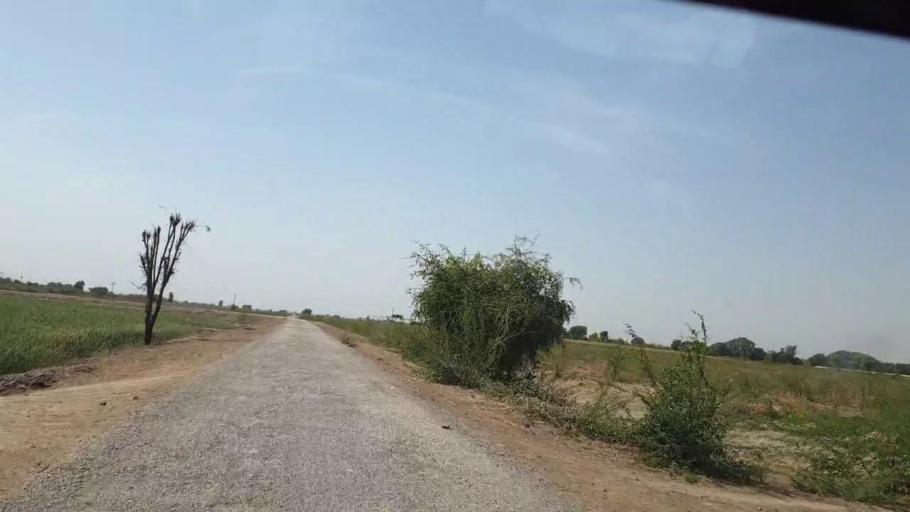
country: PK
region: Sindh
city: Kunri
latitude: 25.1542
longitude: 69.5473
